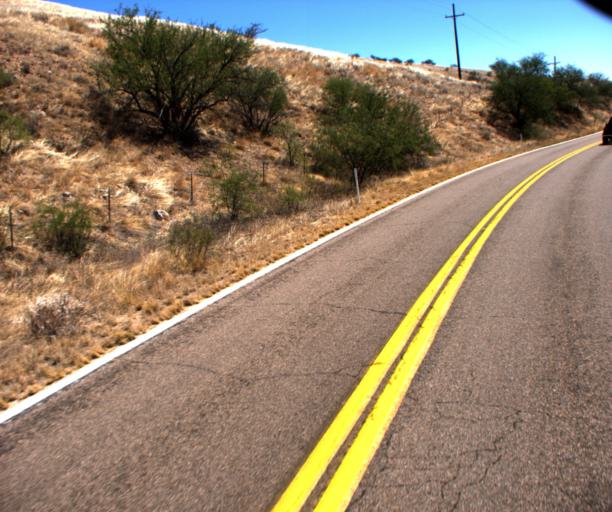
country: US
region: Arizona
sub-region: Santa Cruz County
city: Rio Rico
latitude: 31.3948
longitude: -111.0434
